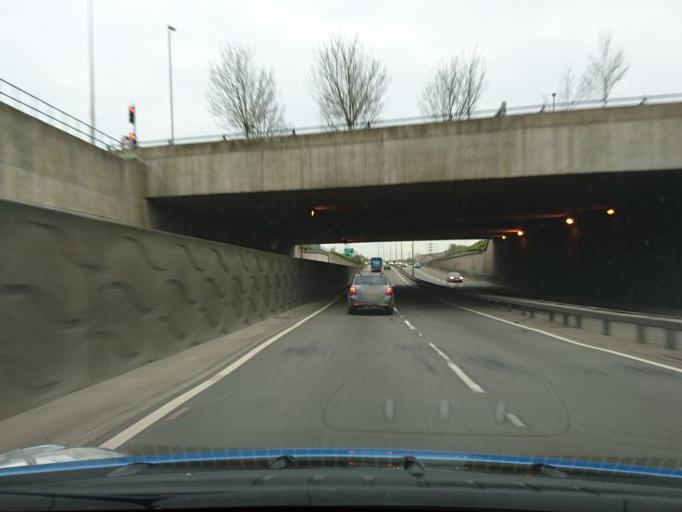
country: GB
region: England
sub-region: Stoke-on-Trent
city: Stoke-on-Trent
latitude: 53.0032
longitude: -2.1795
